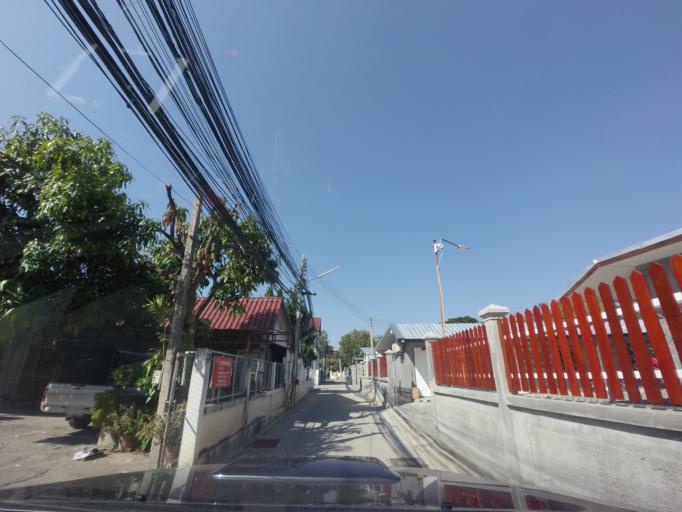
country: TH
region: Chiang Mai
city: Chiang Mai
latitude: 18.7726
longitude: 98.9786
